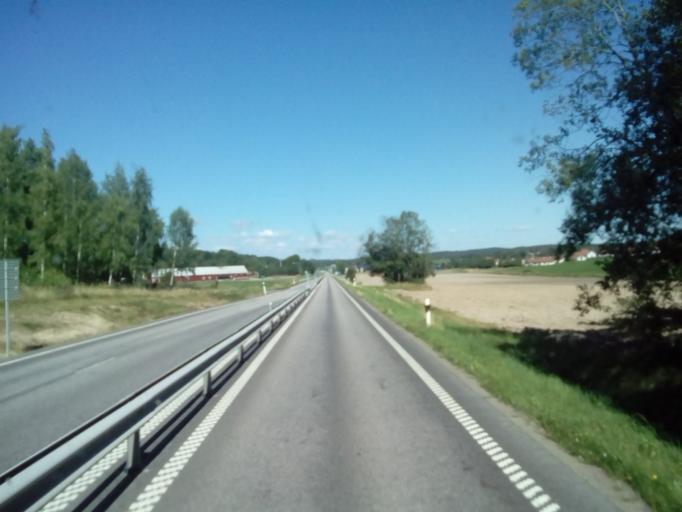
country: SE
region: OEstergoetland
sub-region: Kinda Kommun
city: Rimforsa
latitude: 58.1255
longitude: 15.6731
